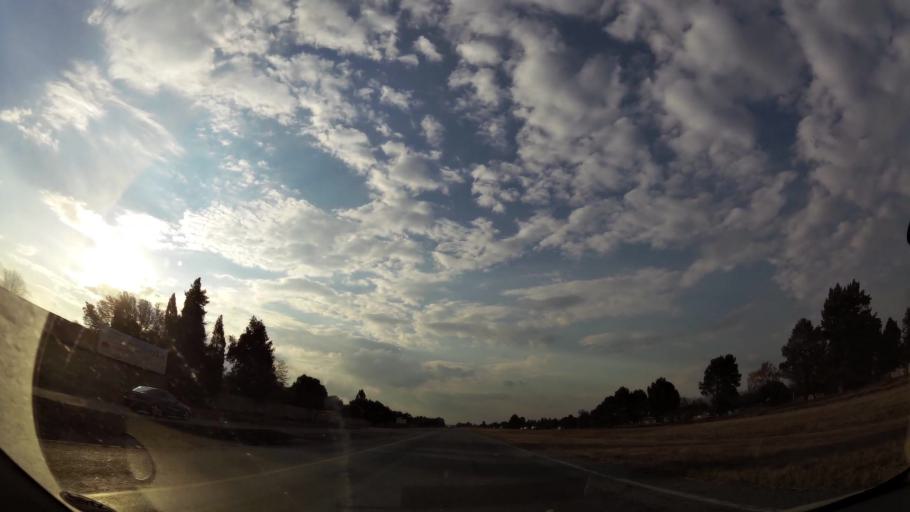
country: ZA
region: Gauteng
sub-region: Sedibeng District Municipality
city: Vanderbijlpark
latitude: -26.7372
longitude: 27.8227
